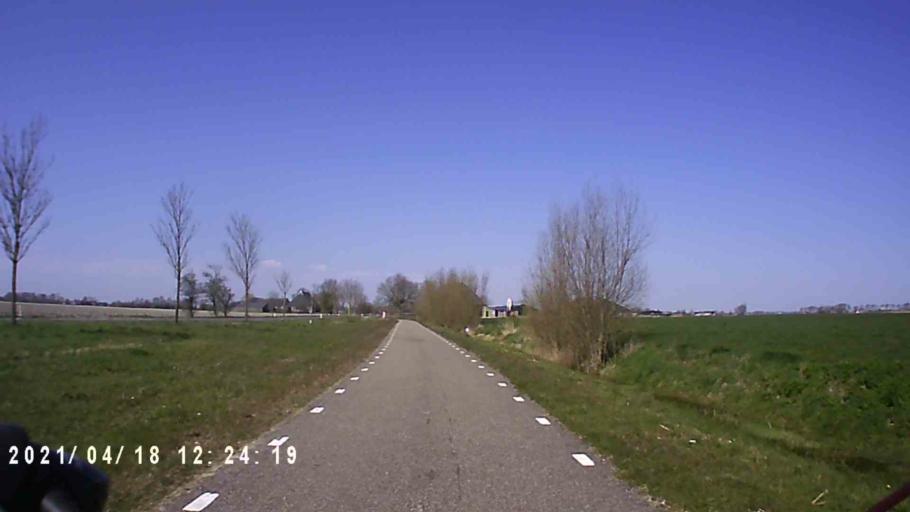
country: NL
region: Friesland
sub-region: Gemeente Dongeradeel
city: Anjum
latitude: 53.3274
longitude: 6.1185
